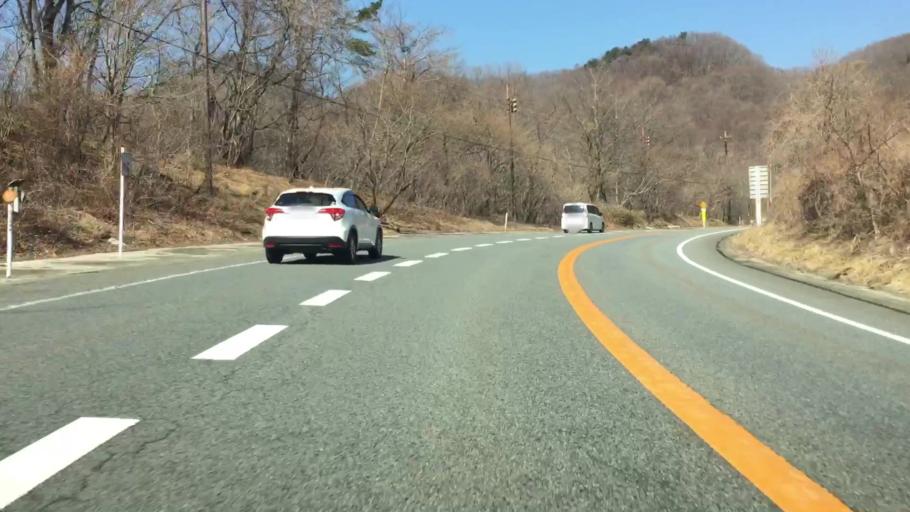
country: JP
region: Nagano
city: Saku
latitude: 36.3033
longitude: 138.6694
